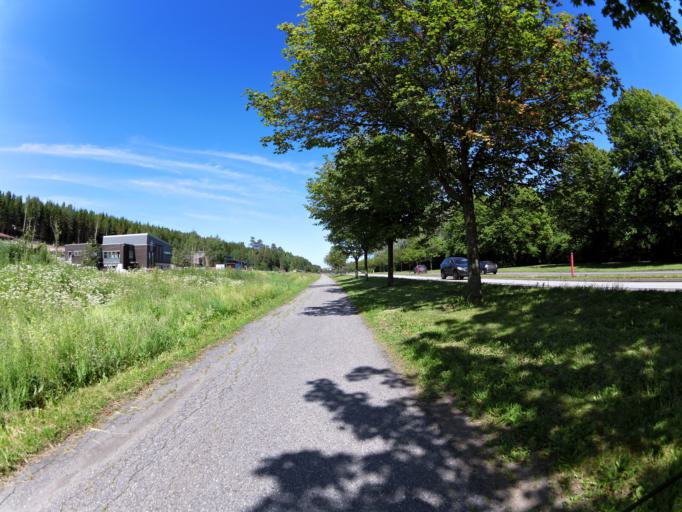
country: NO
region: Ostfold
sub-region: Fredrikstad
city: Fredrikstad
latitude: 59.2276
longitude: 10.9555
